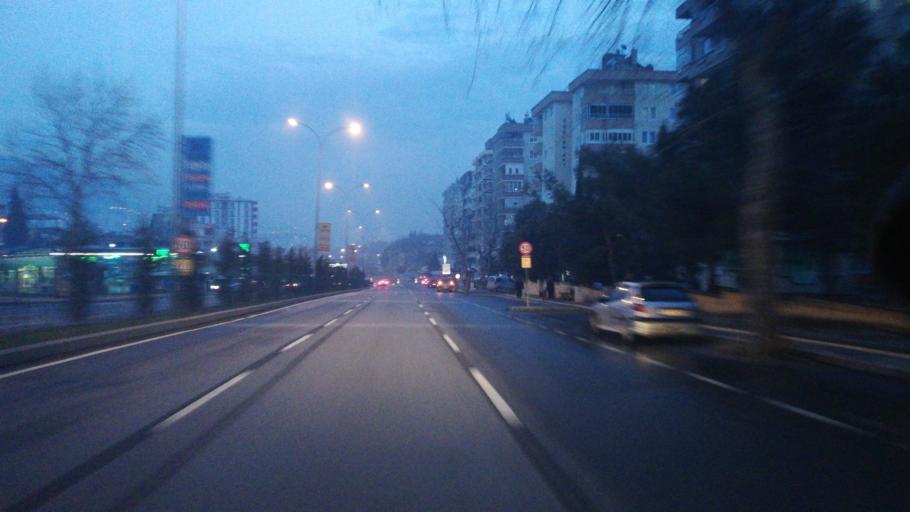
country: TR
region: Kahramanmaras
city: Kahramanmaras
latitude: 37.5840
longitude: 36.9115
